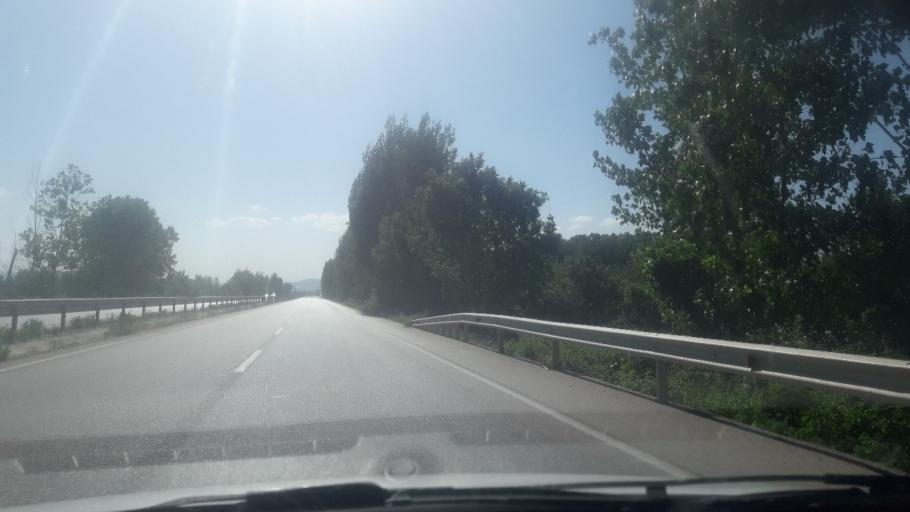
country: TR
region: Tokat
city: Dokmetepe
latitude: 40.3134
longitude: 36.2725
